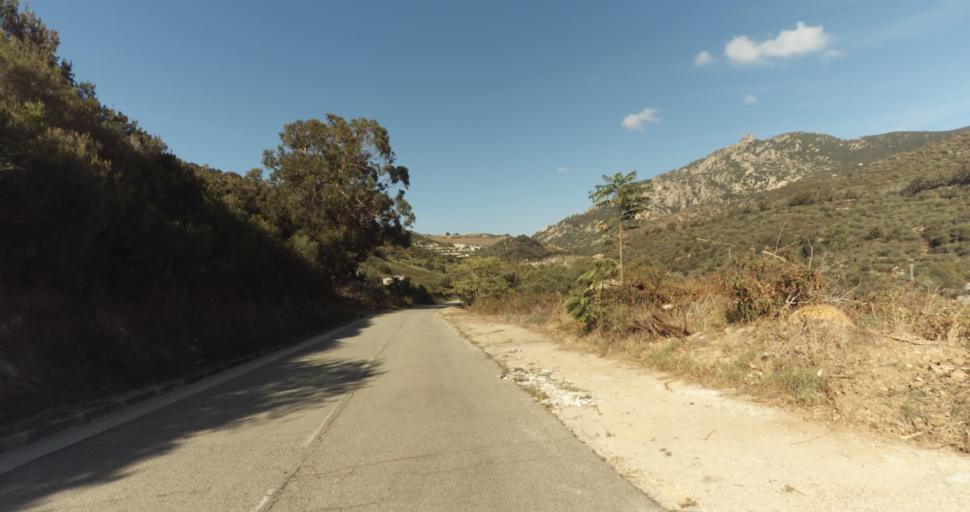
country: FR
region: Corsica
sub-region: Departement de la Corse-du-Sud
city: Ajaccio
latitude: 41.9278
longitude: 8.7048
